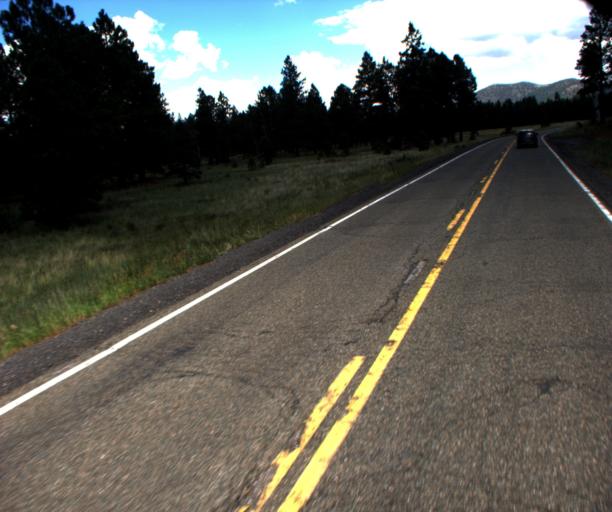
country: US
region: Arizona
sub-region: Coconino County
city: Parks
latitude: 35.3929
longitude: -111.7713
